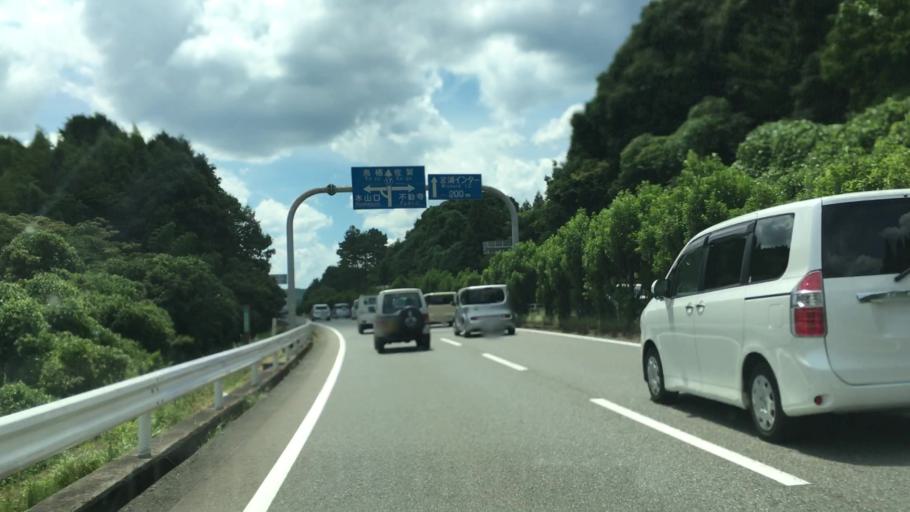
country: JP
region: Saga Prefecture
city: Tosu
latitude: 33.4304
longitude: 130.5199
